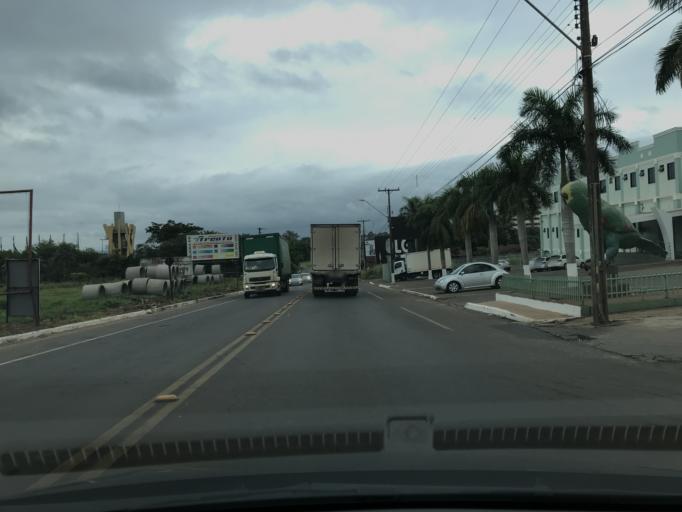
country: PY
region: Canindeyu
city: Salto del Guaira
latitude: -24.0770
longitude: -54.2421
